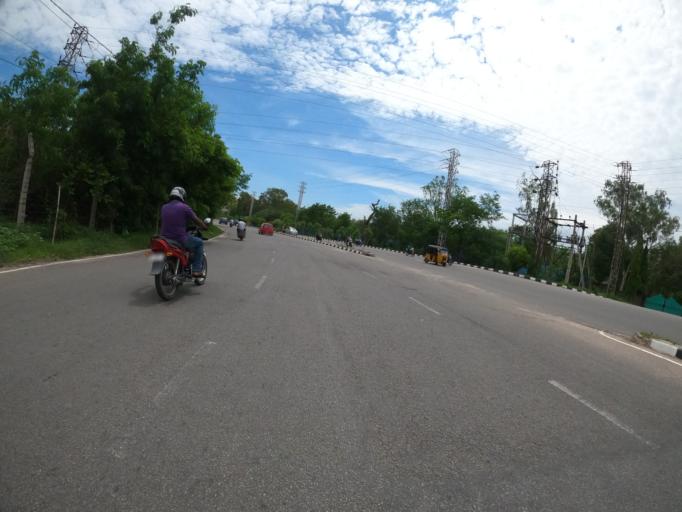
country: IN
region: Telangana
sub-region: Hyderabad
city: Hyderabad
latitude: 17.3688
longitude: 78.4034
